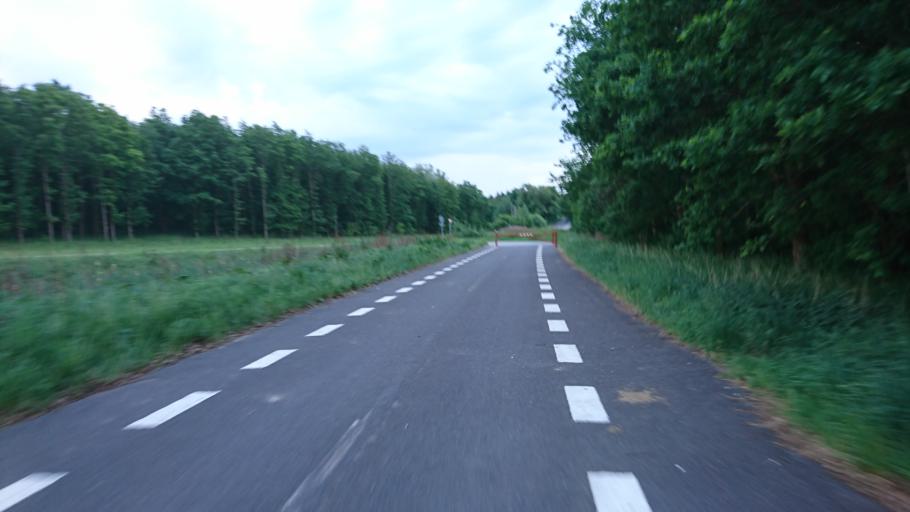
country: DK
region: Capital Region
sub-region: Ballerup Kommune
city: Ballerup
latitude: 55.7054
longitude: 12.3572
